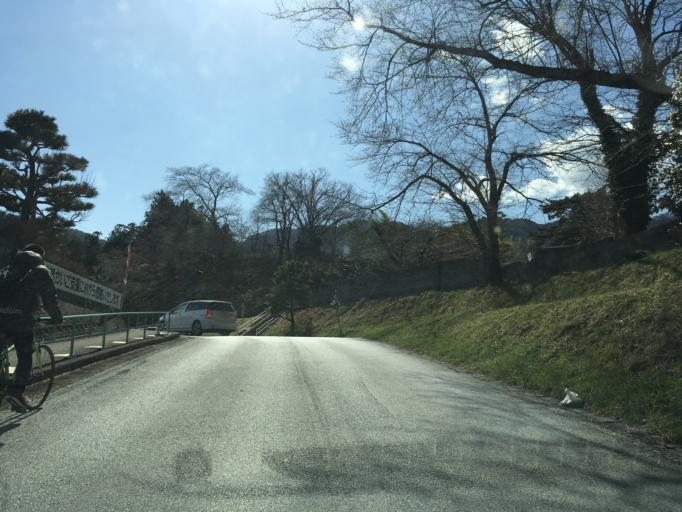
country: JP
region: Iwate
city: Ofunato
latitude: 39.0824
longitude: 141.7077
